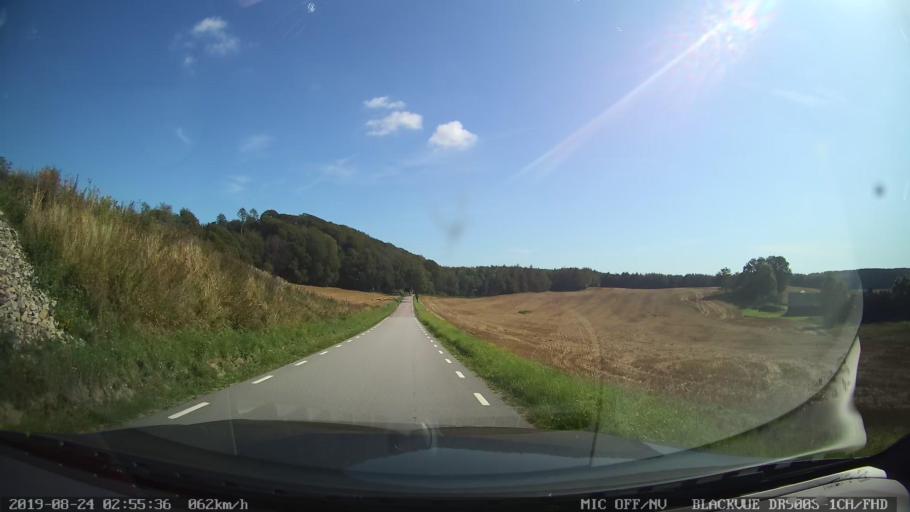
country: SE
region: Skane
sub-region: Trelleborgs Kommun
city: Anderslov
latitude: 55.4944
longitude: 13.3870
